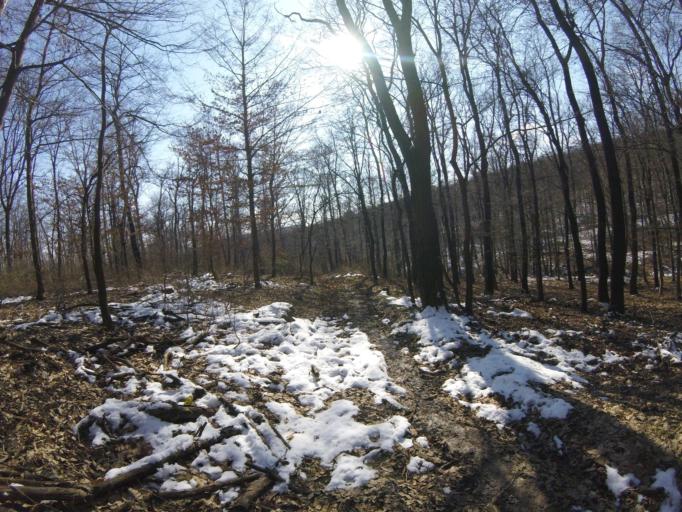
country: HU
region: Pest
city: Pilisszanto
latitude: 47.6653
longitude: 18.8624
